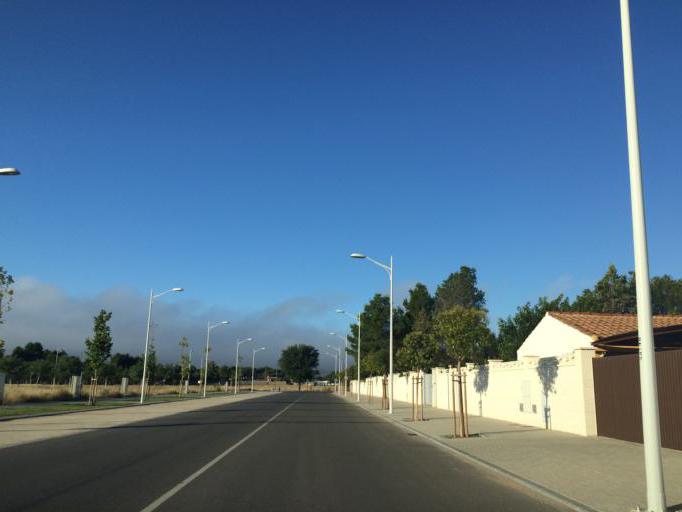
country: ES
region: Castille-La Mancha
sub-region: Provincia de Albacete
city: Albacete
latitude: 39.0034
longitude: -1.8786
